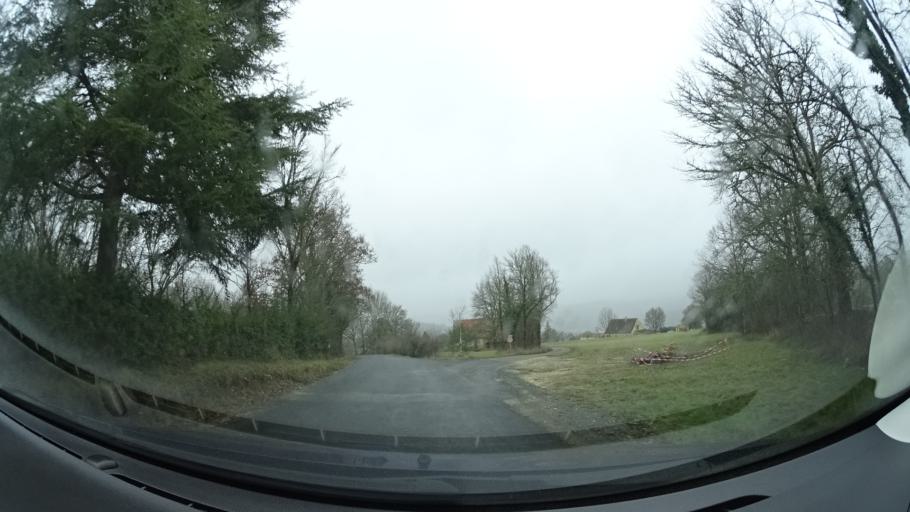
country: FR
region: Aquitaine
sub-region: Departement de la Dordogne
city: Cenac-et-Saint-Julien
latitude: 44.7593
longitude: 1.1675
